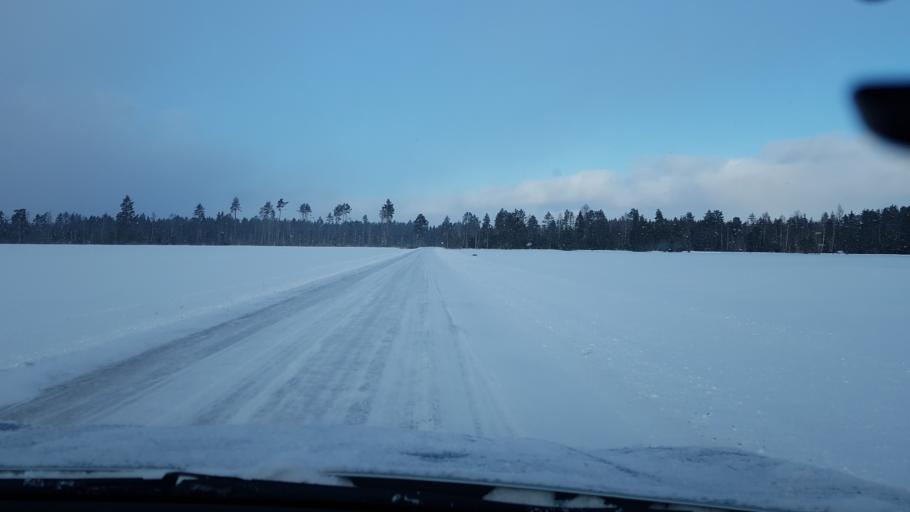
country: EE
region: Harju
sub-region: Nissi vald
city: Turba
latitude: 59.2021
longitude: 24.1400
